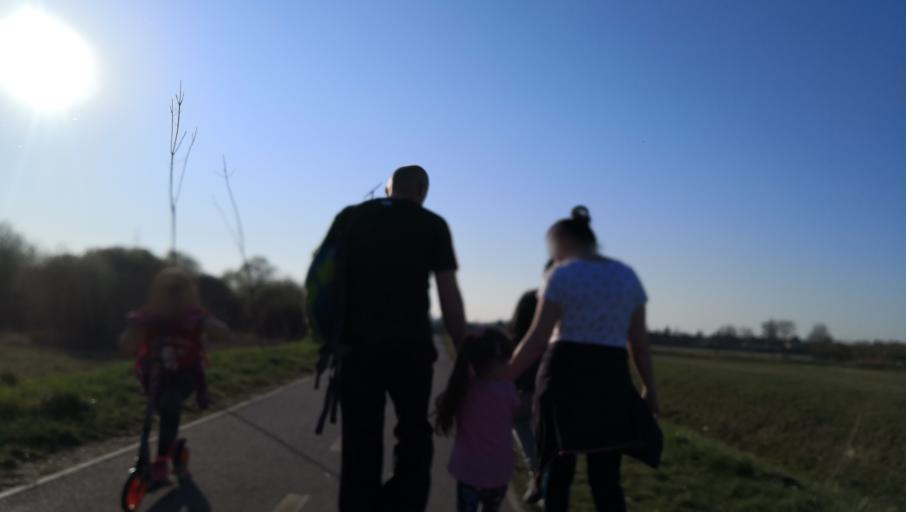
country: HU
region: Pest
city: Csomor
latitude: 47.5133
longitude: 19.2297
